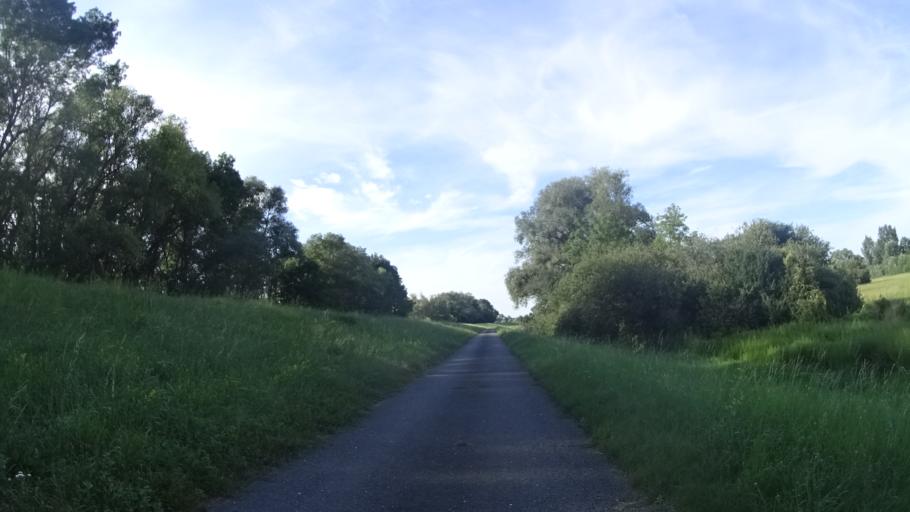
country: AT
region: Lower Austria
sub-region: Politischer Bezirk Ganserndorf
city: Drosing
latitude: 48.5565
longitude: 16.9593
